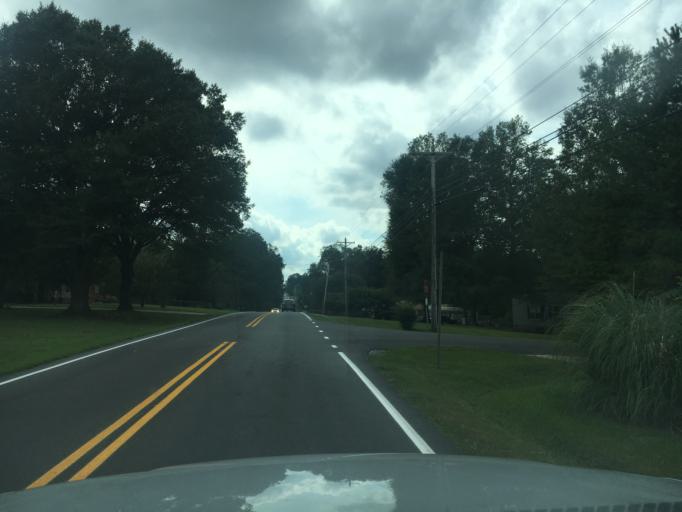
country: US
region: North Carolina
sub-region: Gaston County
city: Bessemer City
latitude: 35.2954
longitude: -81.2330
